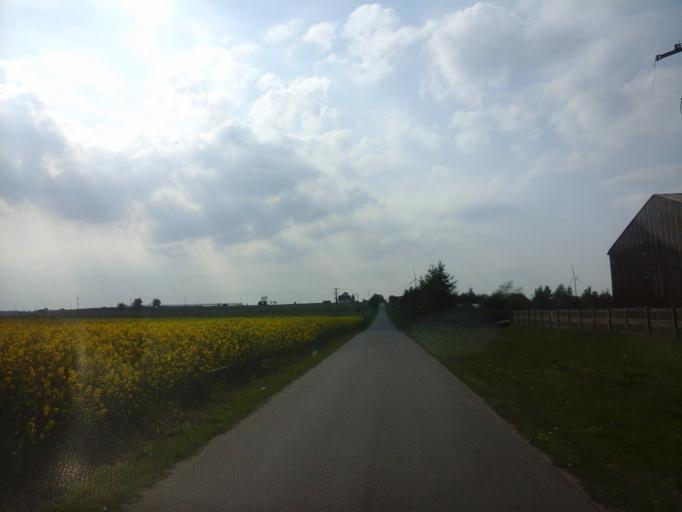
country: PL
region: West Pomeranian Voivodeship
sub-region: Powiat choszczenski
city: Pelczyce
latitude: 53.0264
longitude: 15.2874
